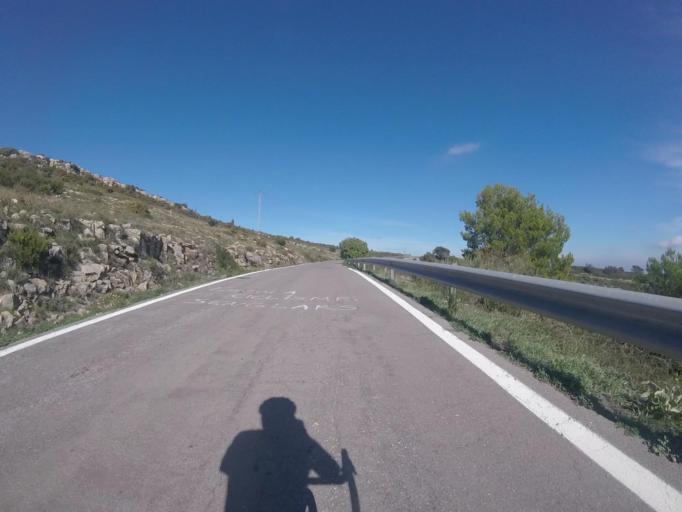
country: ES
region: Valencia
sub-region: Provincia de Castello
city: Sarratella
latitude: 40.3218
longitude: 0.0301
